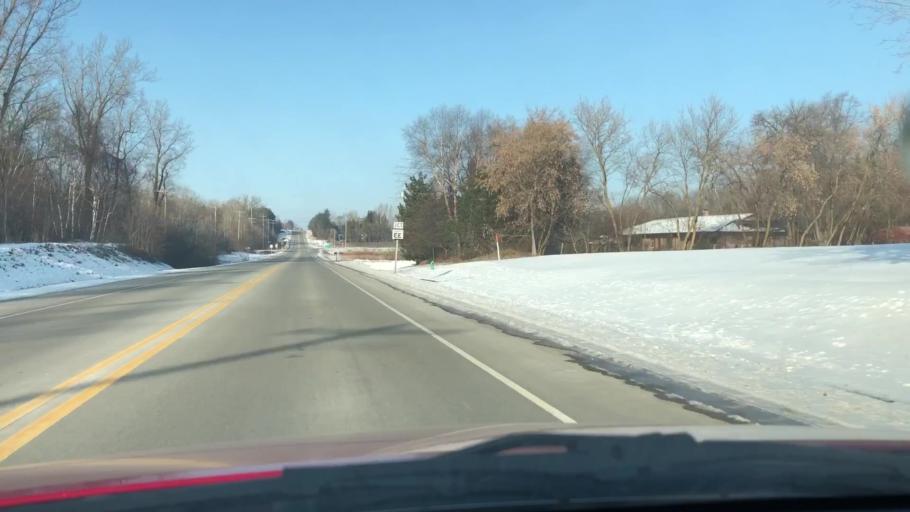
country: US
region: Wisconsin
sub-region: Outagamie County
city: Kimberly
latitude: 44.3222
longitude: -88.3750
